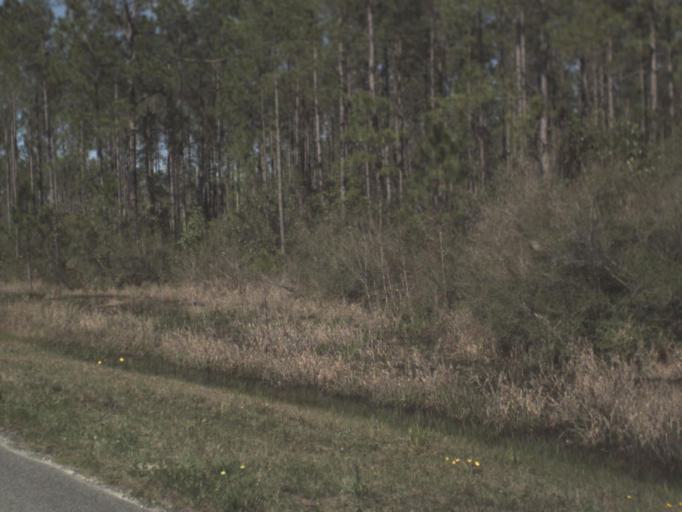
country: US
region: Florida
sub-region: Gulf County
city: Wewahitchka
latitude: 29.9927
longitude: -85.1702
